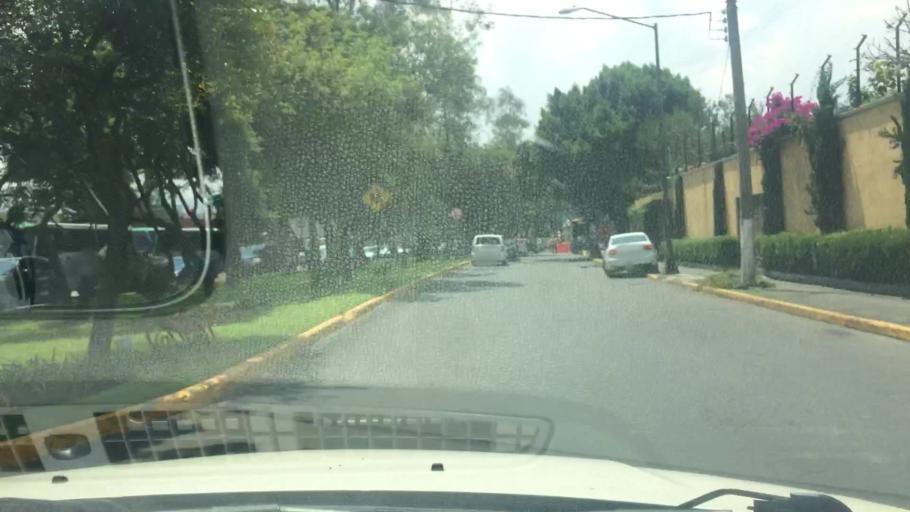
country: MX
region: Mexico City
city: Magdalena Contreras
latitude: 19.3116
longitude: -99.2031
